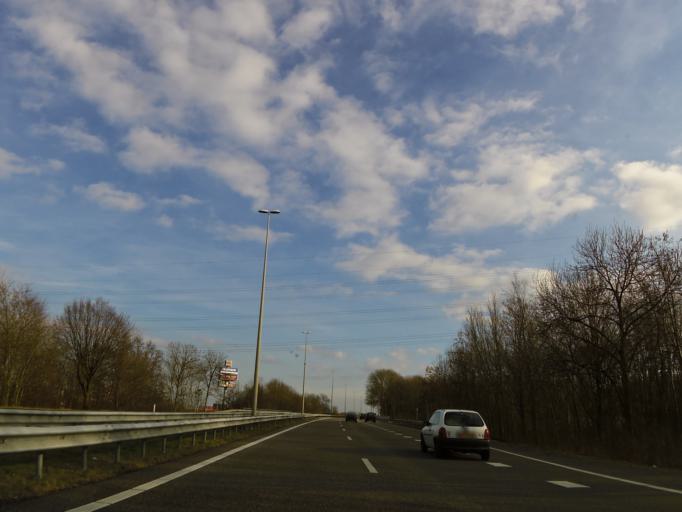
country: NL
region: Limburg
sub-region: Gemeente Simpelveld
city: Simpelveld
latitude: 50.8584
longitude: 5.9982
